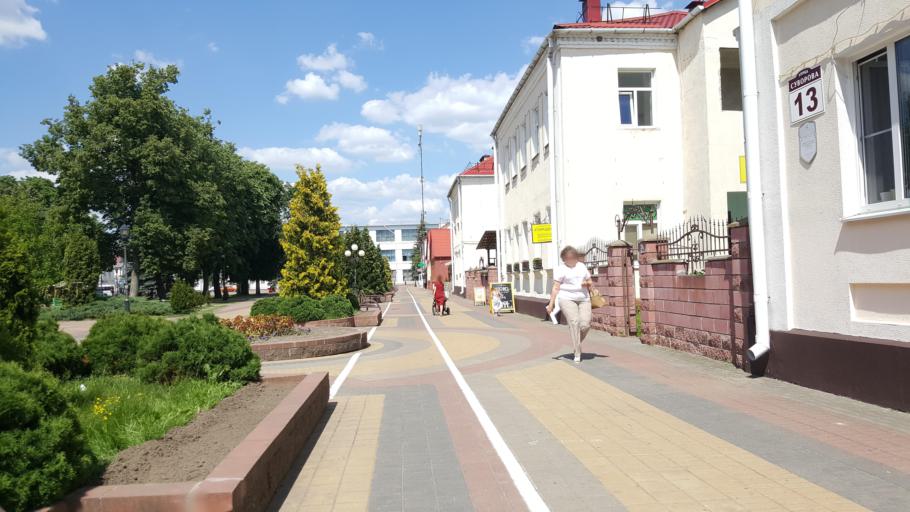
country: BY
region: Brest
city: Kobryn
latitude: 52.2103
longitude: 24.3563
